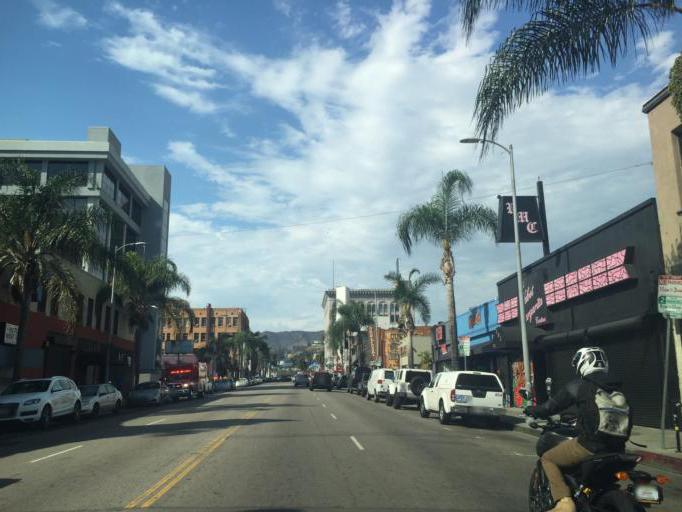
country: US
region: California
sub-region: Los Angeles County
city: Hollywood
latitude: 34.1000
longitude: -118.3295
